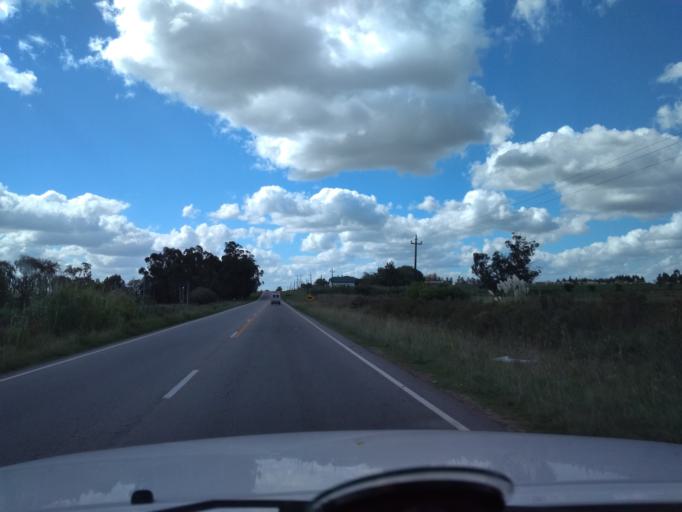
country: UY
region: Canelones
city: Joaquin Suarez
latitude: -34.6983
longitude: -56.0564
